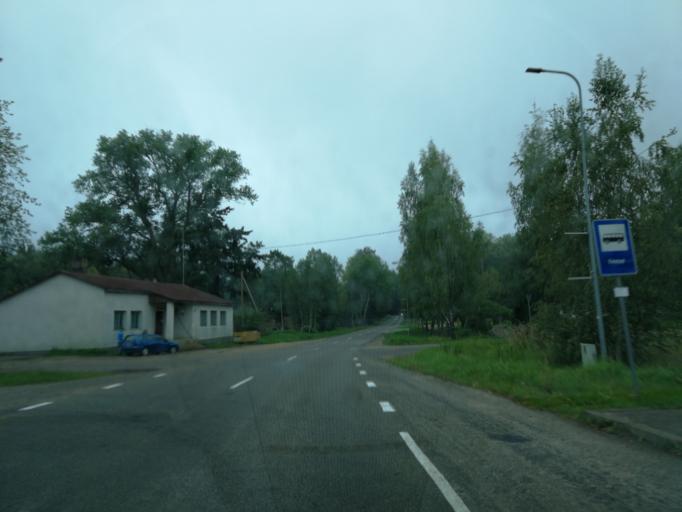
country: LV
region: Preilu Rajons
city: Jaunaglona
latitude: 56.2729
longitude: 27.0436
